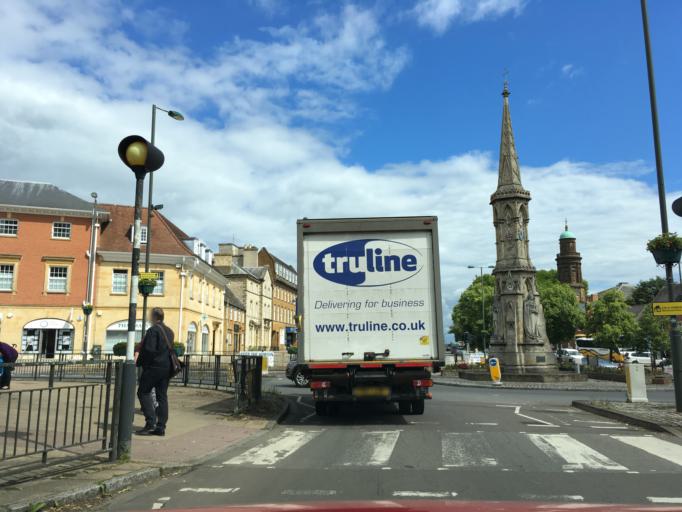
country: GB
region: England
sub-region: Oxfordshire
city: Banbury
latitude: 52.0599
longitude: -1.3404
